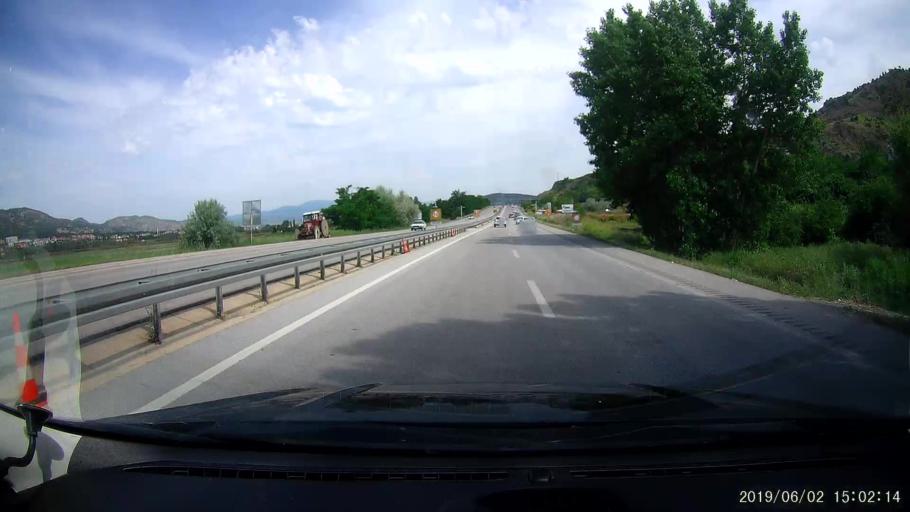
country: TR
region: Corum
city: Osmancik
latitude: 40.9831
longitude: 34.7637
